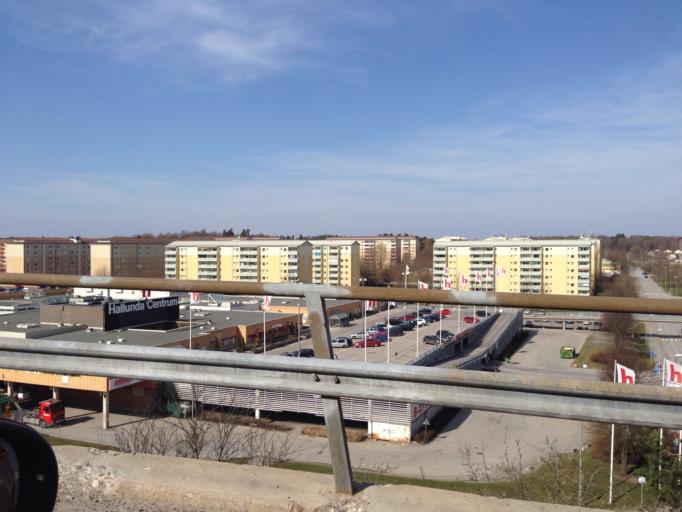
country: SE
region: Stockholm
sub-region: Botkyrka Kommun
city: Eriksberg
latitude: 59.2435
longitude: 17.8287
